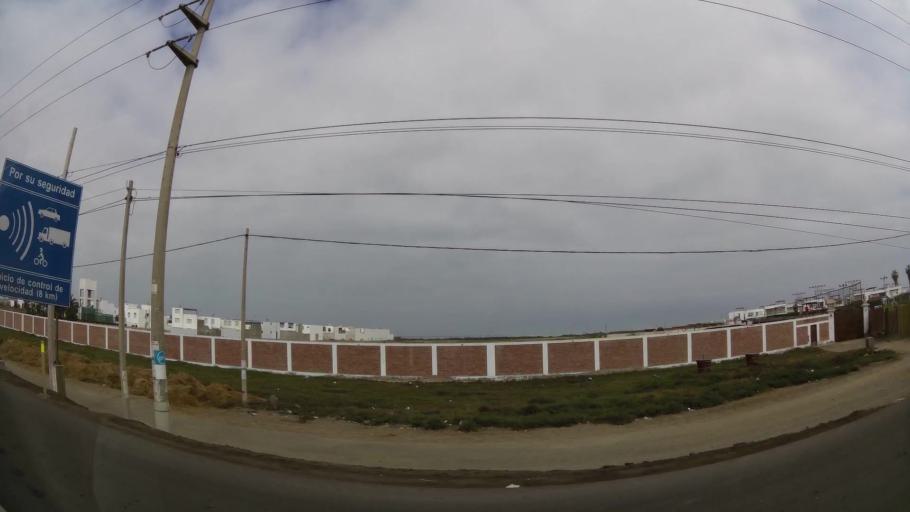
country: PE
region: Lima
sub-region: Provincia de Canete
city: Mala
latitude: -12.7072
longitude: -76.6359
